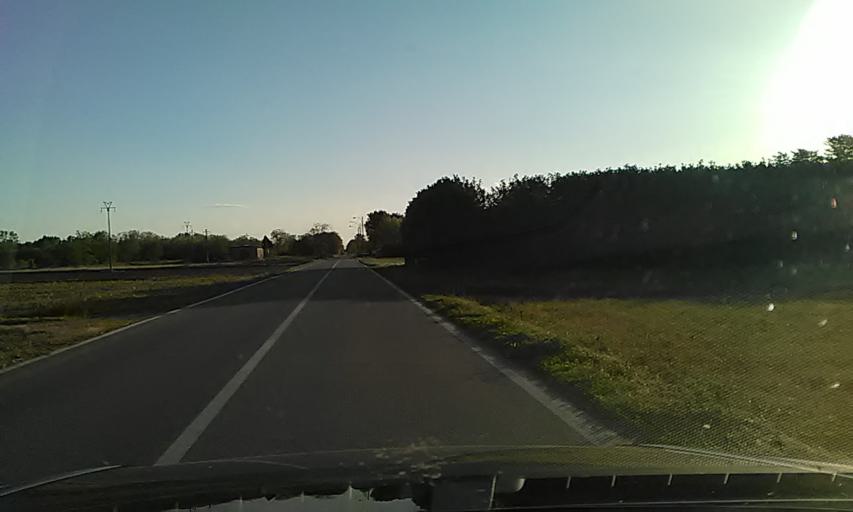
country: IT
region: Piedmont
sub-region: Provincia di Novara
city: Fara Novarese
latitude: 45.5465
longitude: 8.4457
